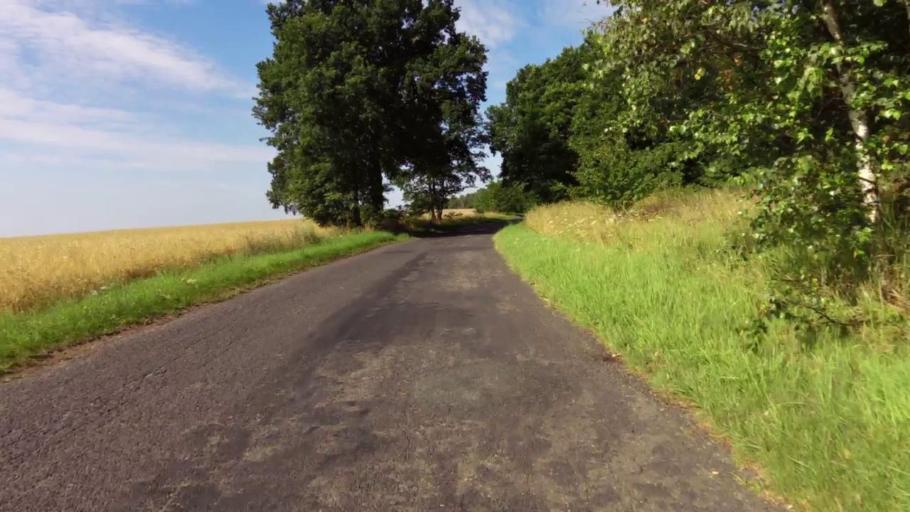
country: PL
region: West Pomeranian Voivodeship
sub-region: Powiat stargardzki
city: Marianowo
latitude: 53.3612
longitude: 15.2243
